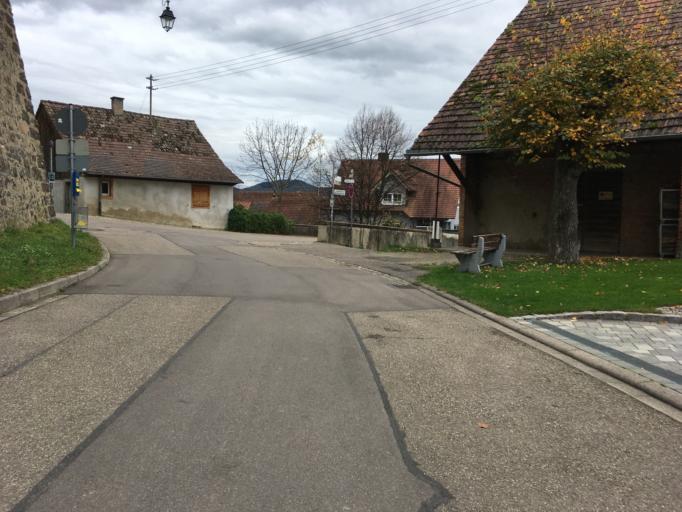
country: DE
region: Baden-Wuerttemberg
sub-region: Freiburg Region
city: Sasbach
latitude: 48.0995
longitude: 7.5963
